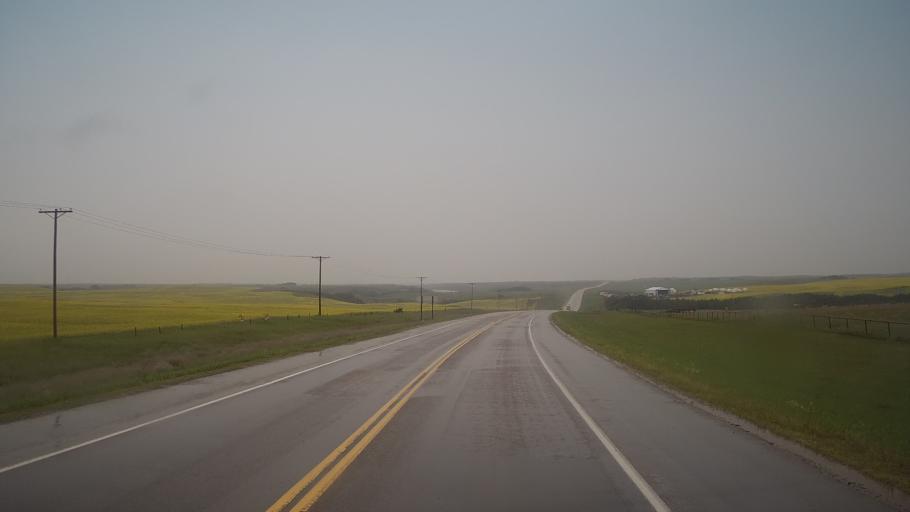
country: CA
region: Saskatchewan
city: Biggar
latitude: 52.0674
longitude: -108.0029
